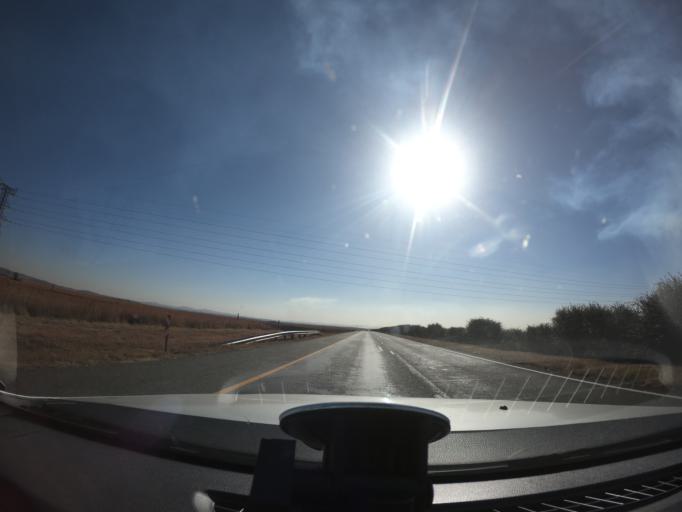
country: ZA
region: Gauteng
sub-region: Sedibeng District Municipality
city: Heidelberg
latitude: -26.4373
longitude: 28.3025
